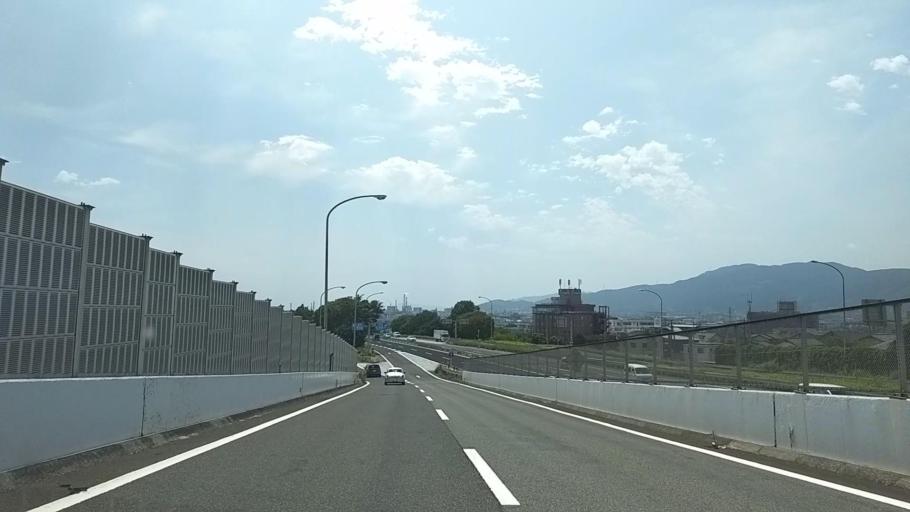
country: JP
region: Shizuoka
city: Fuji
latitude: 35.1752
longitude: 138.6758
